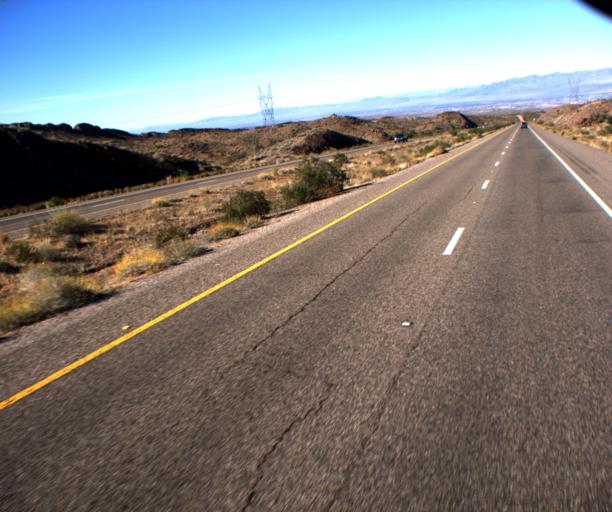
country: US
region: Nevada
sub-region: Clark County
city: Laughlin
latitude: 35.1903
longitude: -114.4460
